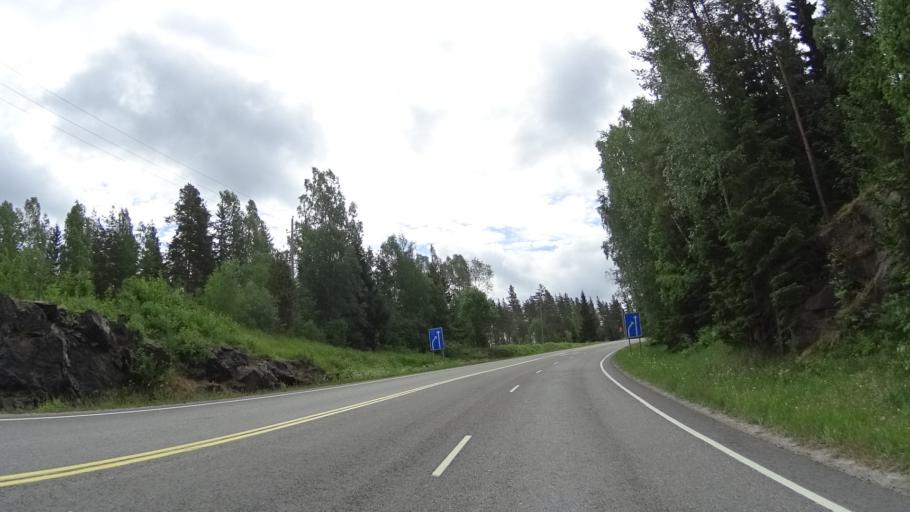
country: FI
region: Uusimaa
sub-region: Helsinki
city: Vihti
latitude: 60.2921
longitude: 24.4040
